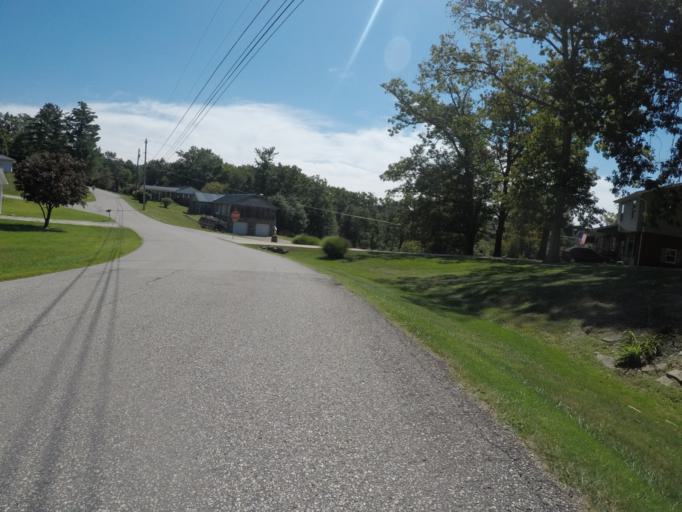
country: US
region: Kentucky
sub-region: Boyd County
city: Meads
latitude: 38.4116
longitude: -82.6578
